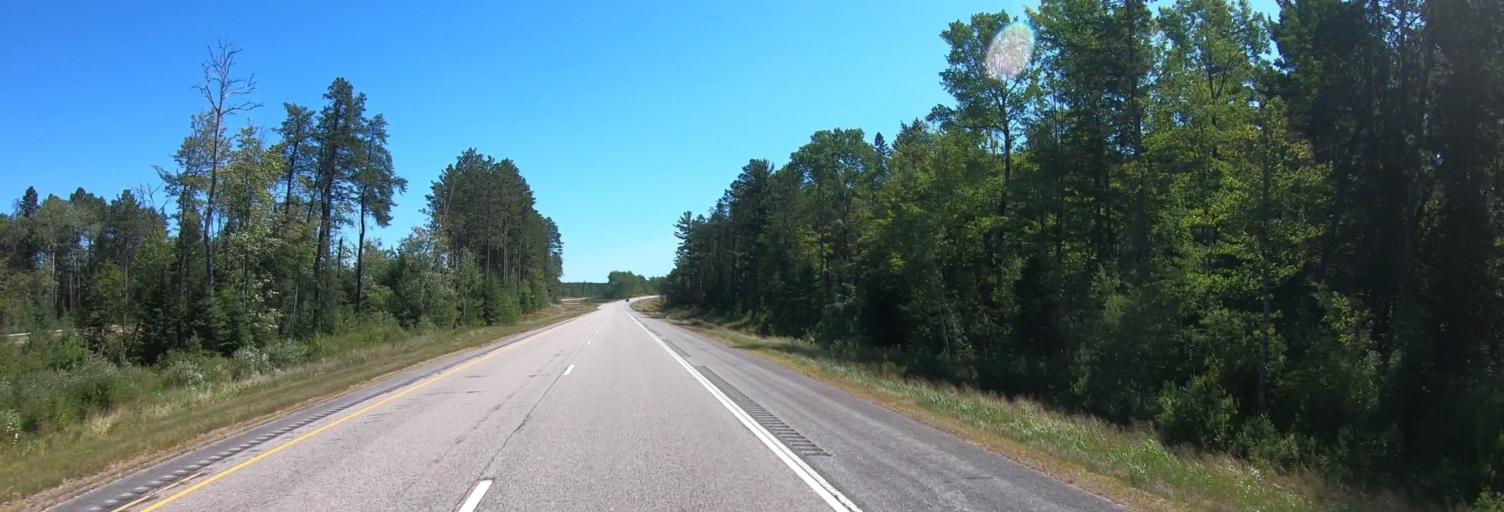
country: US
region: Minnesota
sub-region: Saint Louis County
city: Mountain Iron
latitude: 47.6604
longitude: -92.5995
